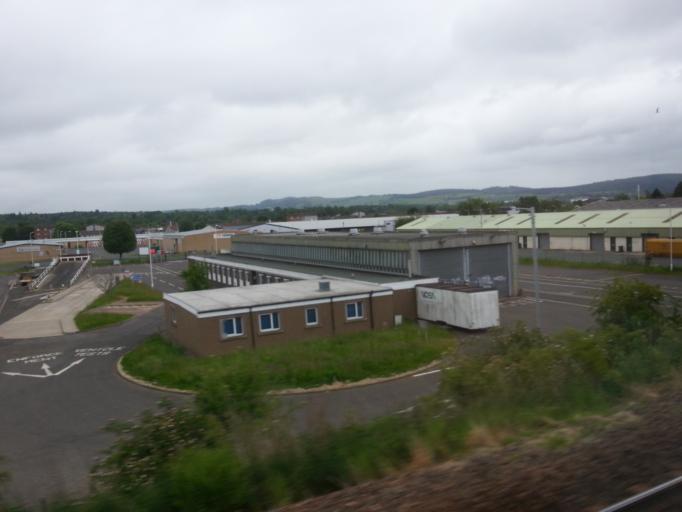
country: GB
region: Scotland
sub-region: Perth and Kinross
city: Luncarty
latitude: 56.4172
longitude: -3.4613
